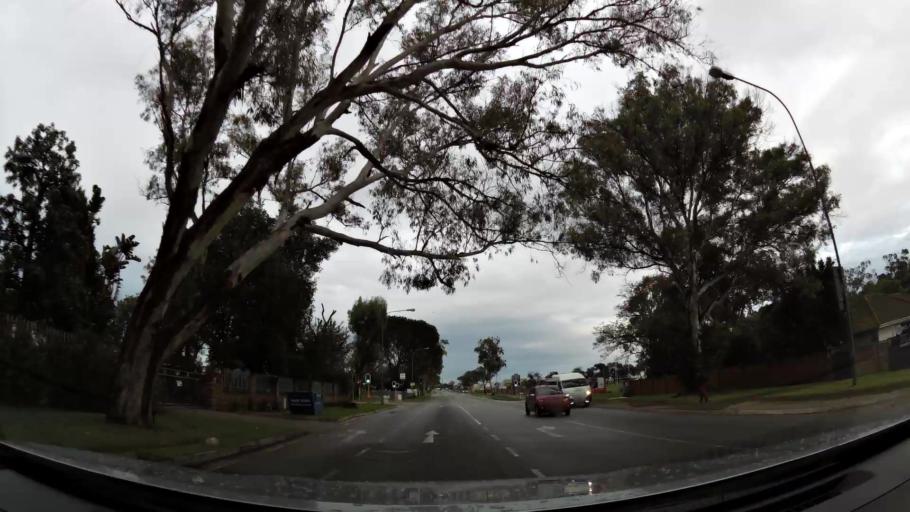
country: ZA
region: Eastern Cape
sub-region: Nelson Mandela Bay Metropolitan Municipality
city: Port Elizabeth
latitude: -33.9820
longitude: 25.5644
